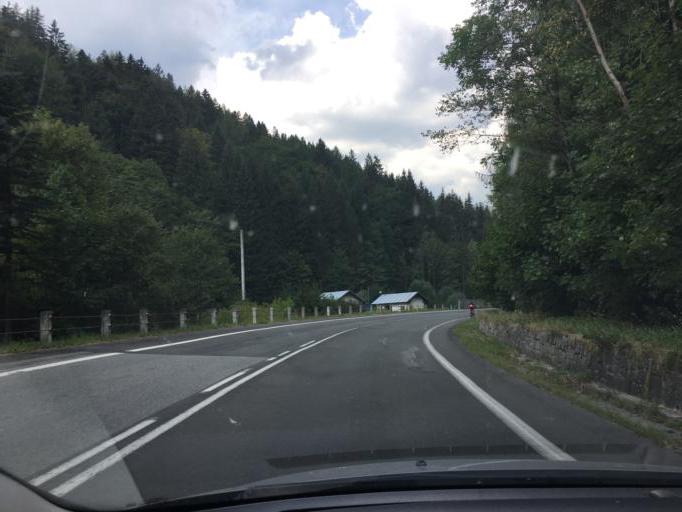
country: CZ
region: Kralovehradecky
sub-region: Okres Trutnov
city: Vrchlabi
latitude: 50.6637
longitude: 15.5943
